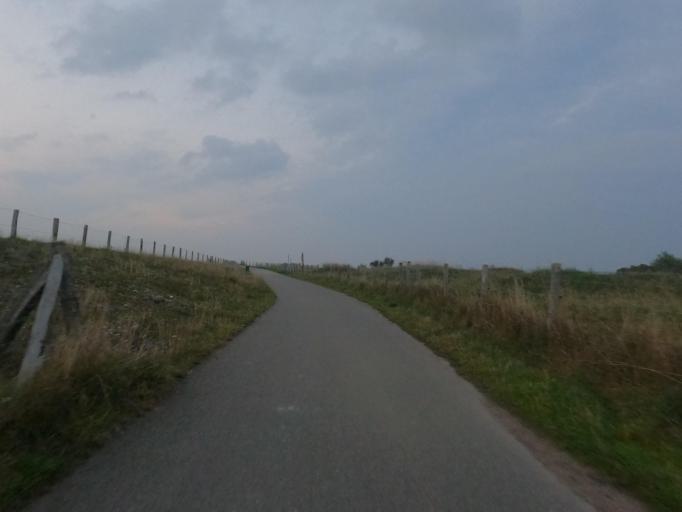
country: DE
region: Schleswig-Holstein
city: Dahme
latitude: 54.2589
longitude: 11.0812
